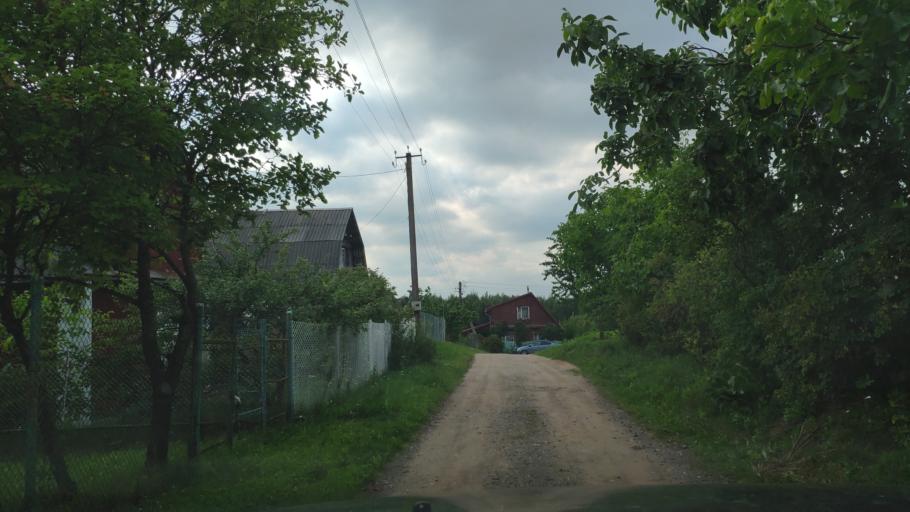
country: BY
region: Minsk
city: Khatsyezhyna
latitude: 53.8561
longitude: 27.2907
